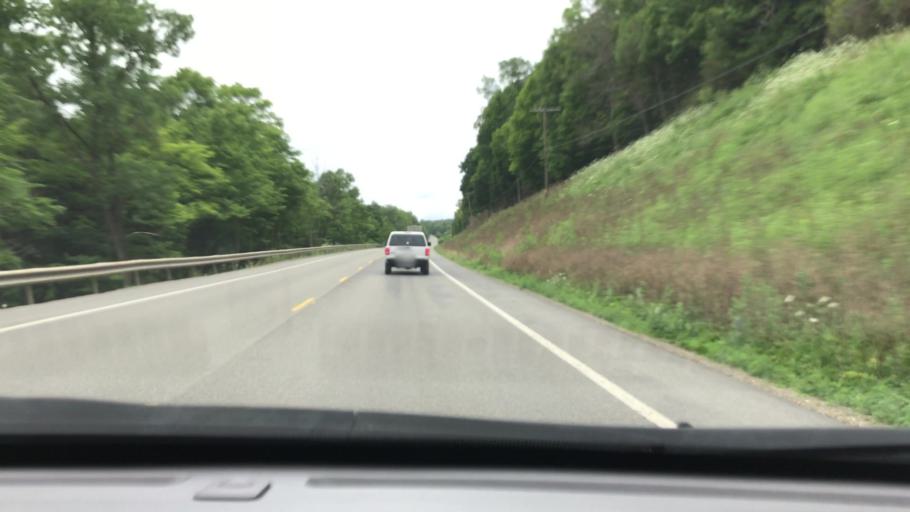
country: US
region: Pennsylvania
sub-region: McKean County
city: Kane
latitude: 41.6882
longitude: -78.6897
